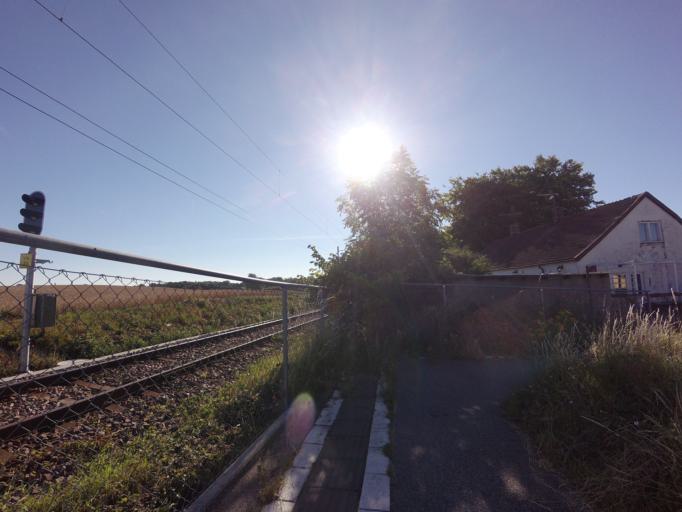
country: SE
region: Skane
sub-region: Ystads Kommun
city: Ystad
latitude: 55.4284
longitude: 13.7197
